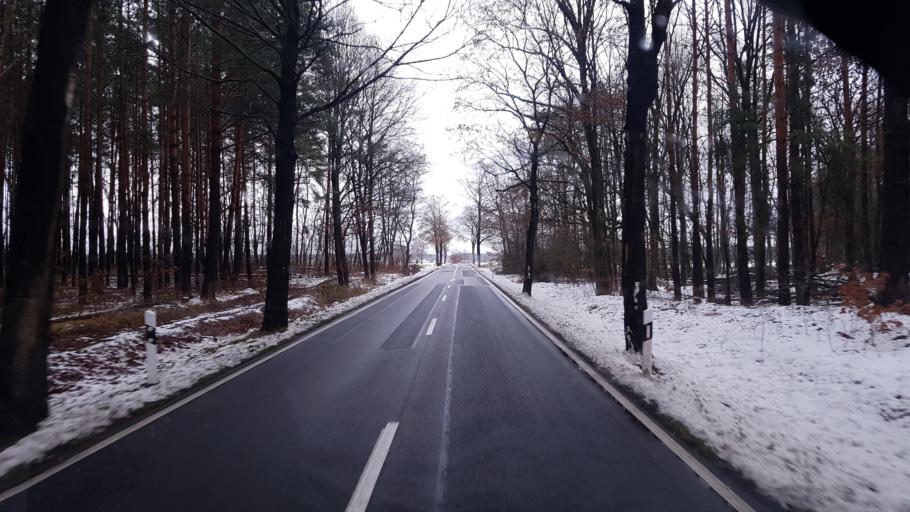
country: DE
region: Brandenburg
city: Tauer
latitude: 51.9788
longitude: 14.5105
